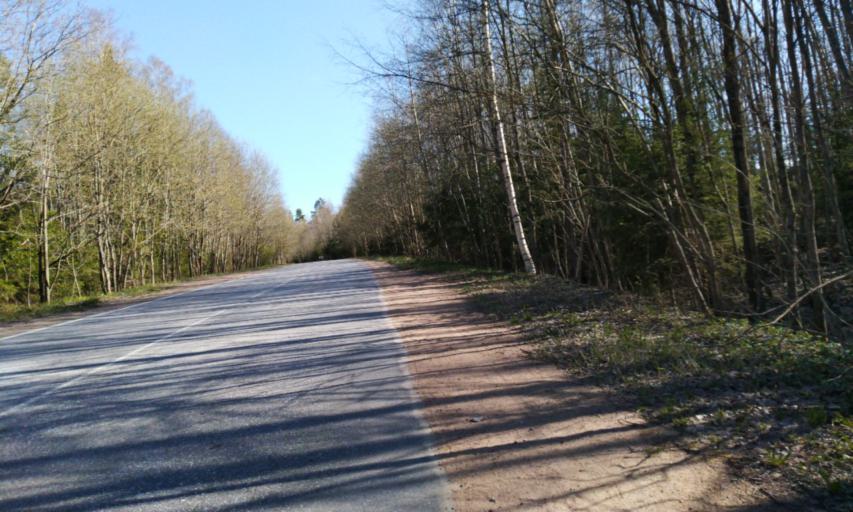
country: RU
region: Leningrad
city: Garbolovo
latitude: 60.3852
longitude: 30.4728
